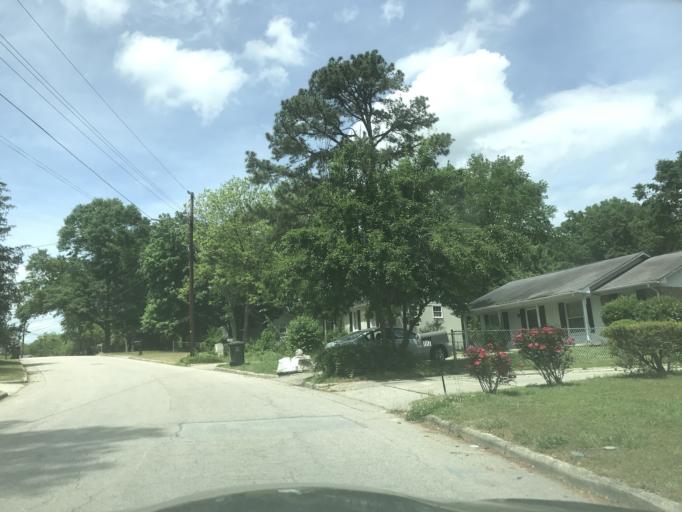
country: US
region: North Carolina
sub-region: Wake County
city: Raleigh
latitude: 35.7623
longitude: -78.5897
